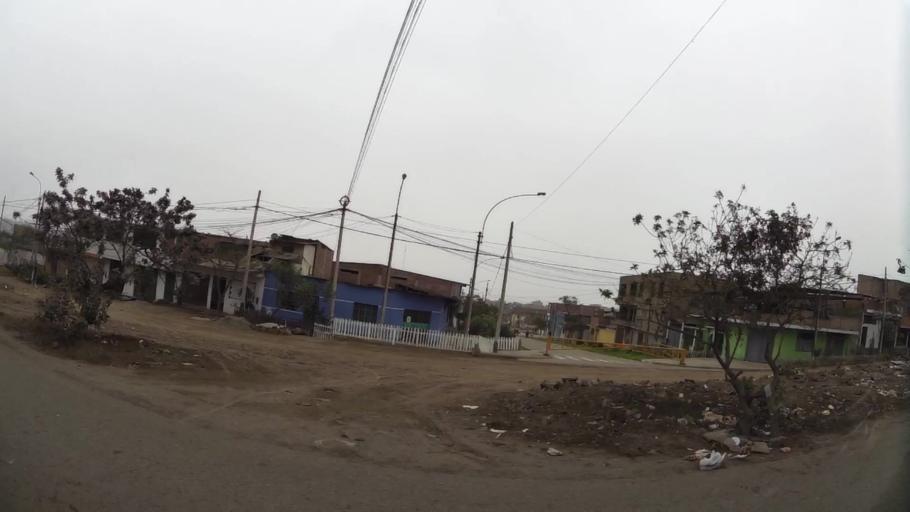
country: PE
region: Lima
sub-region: Lima
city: Surco
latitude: -12.1845
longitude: -76.9230
